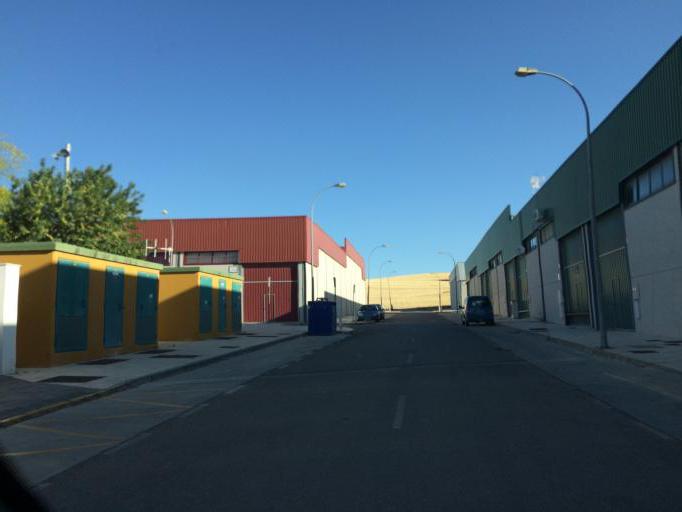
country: ES
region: Andalusia
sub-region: Provincia de Malaga
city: Campillos
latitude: 37.0505
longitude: -4.8750
